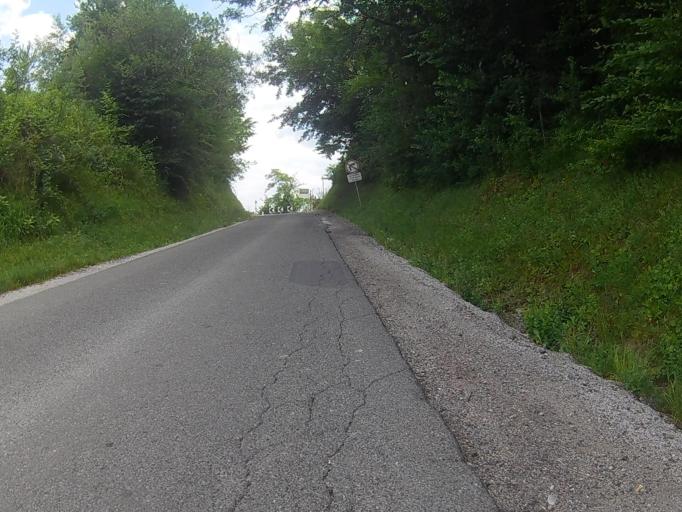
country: SI
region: Kungota
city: Zgornja Kungota
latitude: 46.6569
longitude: 15.6334
